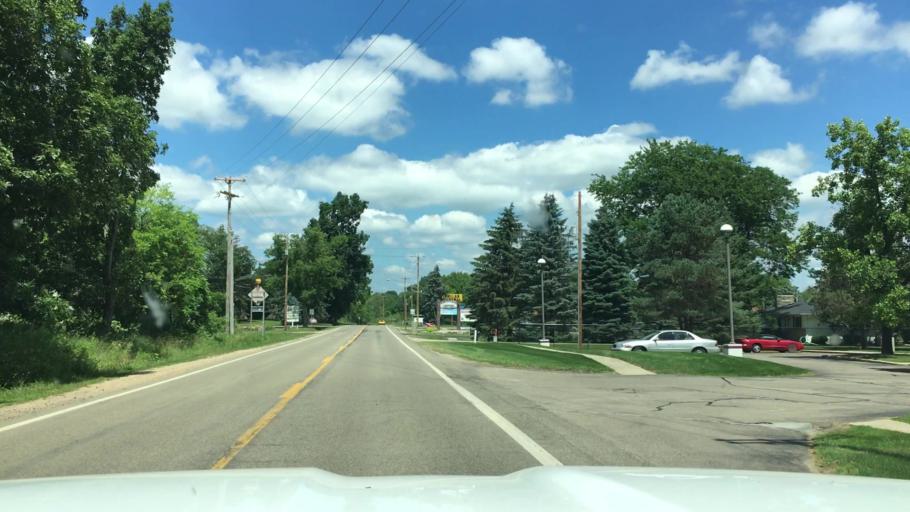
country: US
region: Michigan
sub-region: Barry County
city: Stony Point
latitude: 42.5053
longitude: -85.4088
